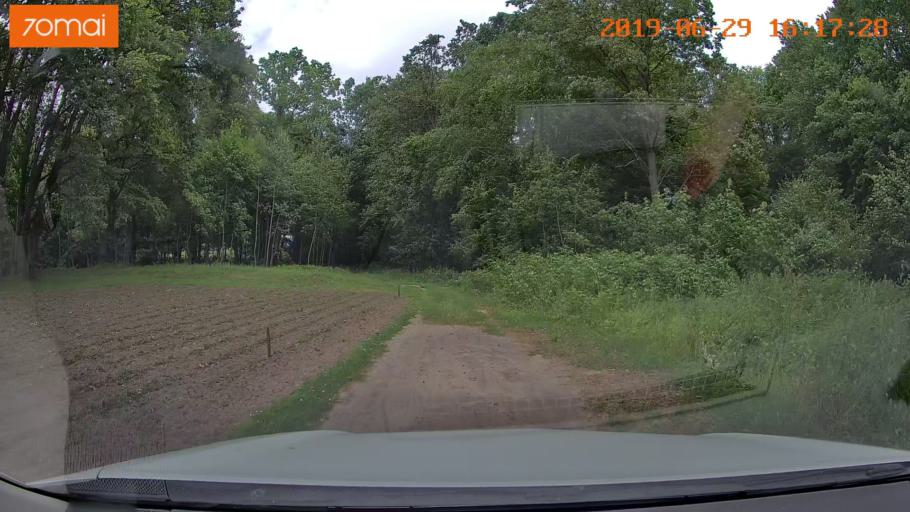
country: BY
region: Brest
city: Luninyets
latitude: 52.1996
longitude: 27.0116
